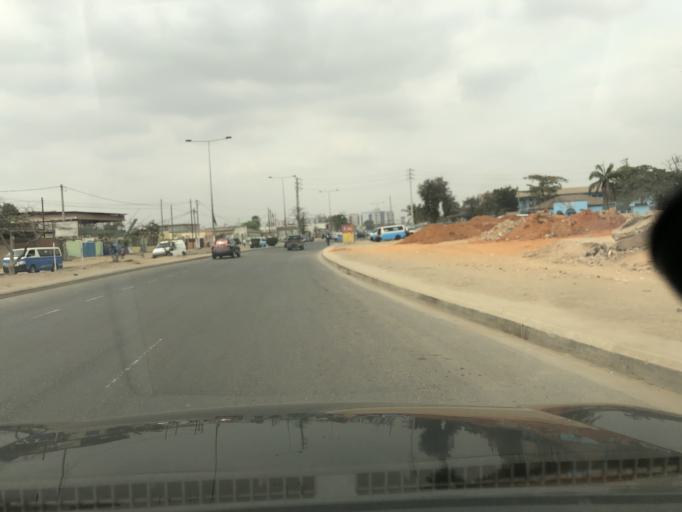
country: AO
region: Luanda
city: Luanda
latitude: -8.8409
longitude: 13.2839
